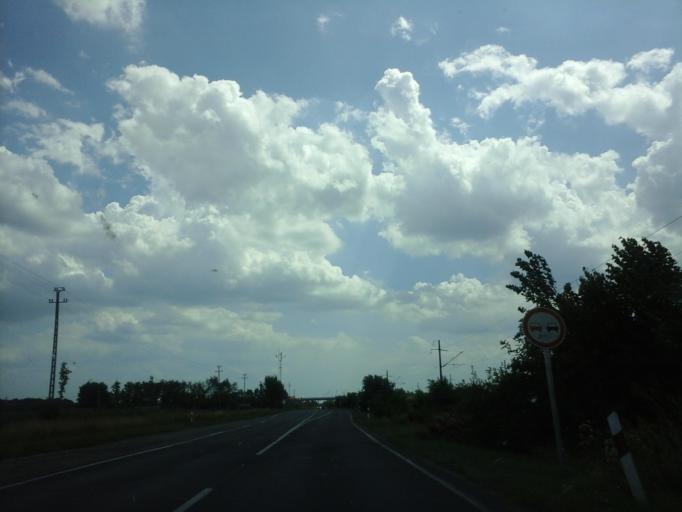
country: HU
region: Gyor-Moson-Sopron
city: Rajka
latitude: 48.0084
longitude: 17.1834
